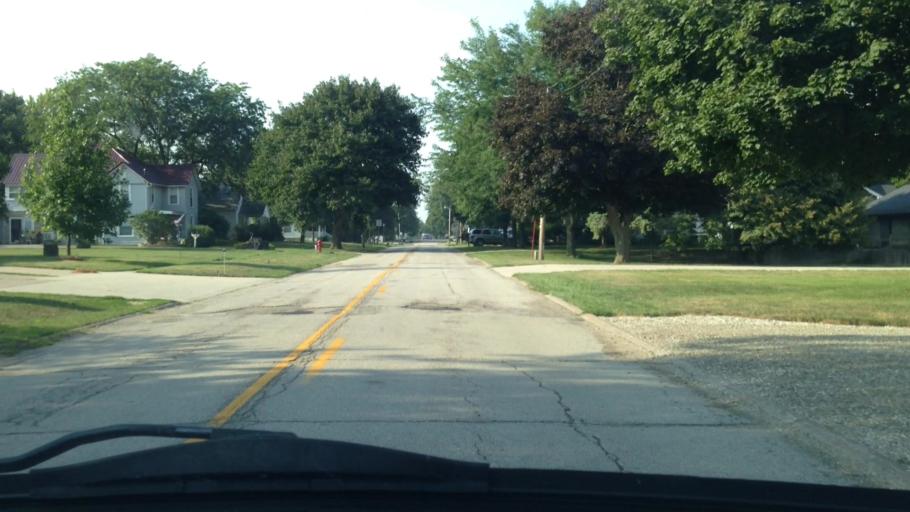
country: US
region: Iowa
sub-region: Henry County
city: Winfield
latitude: 41.2109
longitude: -91.5388
